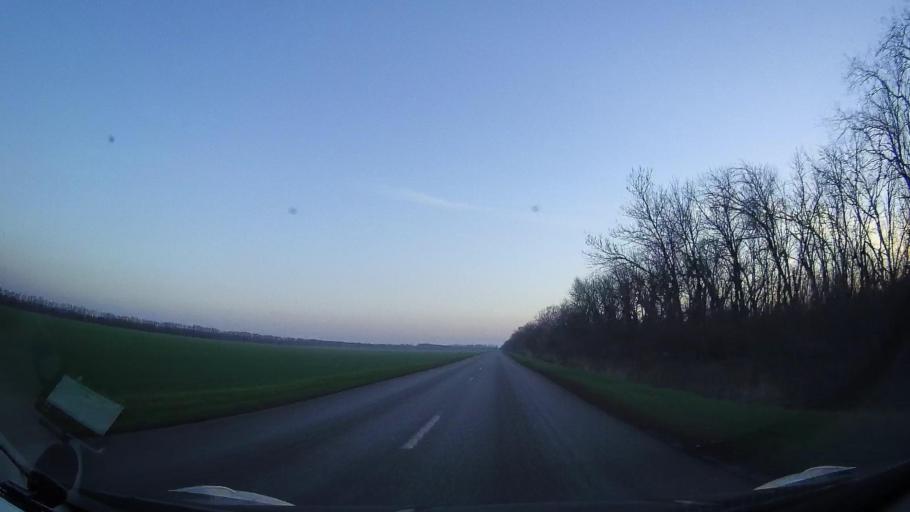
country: RU
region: Rostov
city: Zernograd
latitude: 46.9809
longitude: 40.3915
